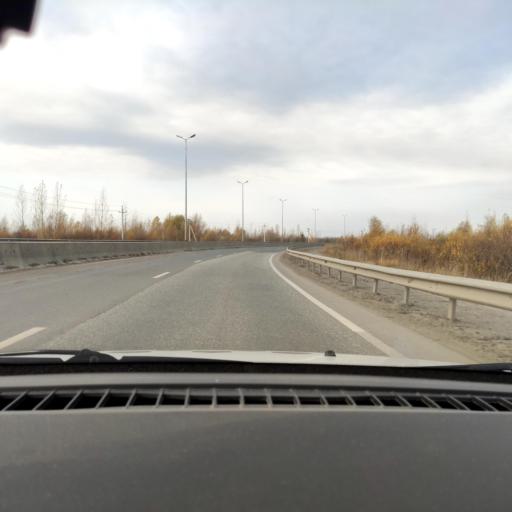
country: RU
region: Perm
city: Kondratovo
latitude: 57.9998
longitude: 56.0984
